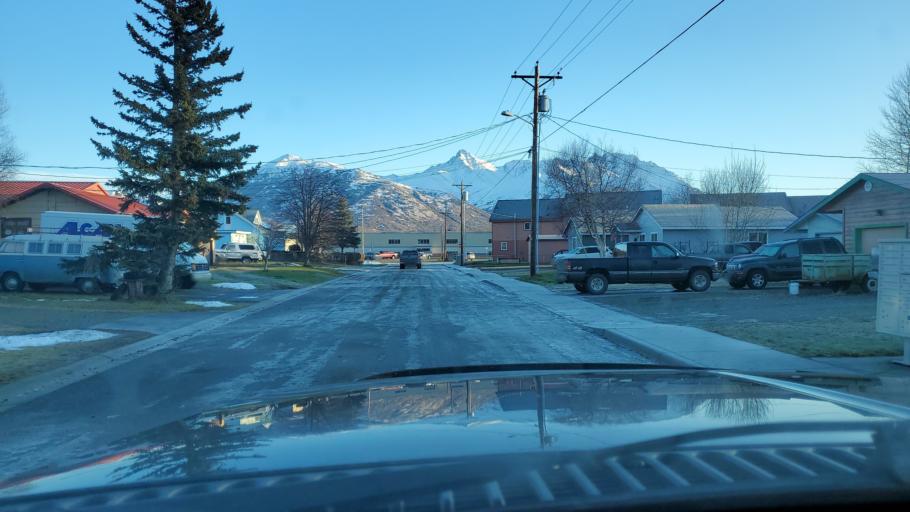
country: US
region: Alaska
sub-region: Matanuska-Susitna Borough
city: Palmer
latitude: 61.6109
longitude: -149.1054
